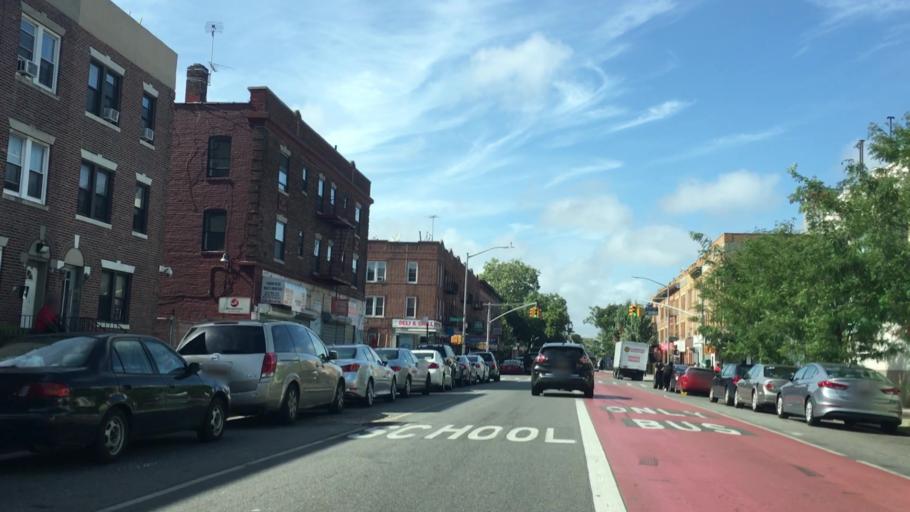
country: US
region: New York
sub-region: Kings County
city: Brooklyn
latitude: 40.6547
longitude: -73.9529
